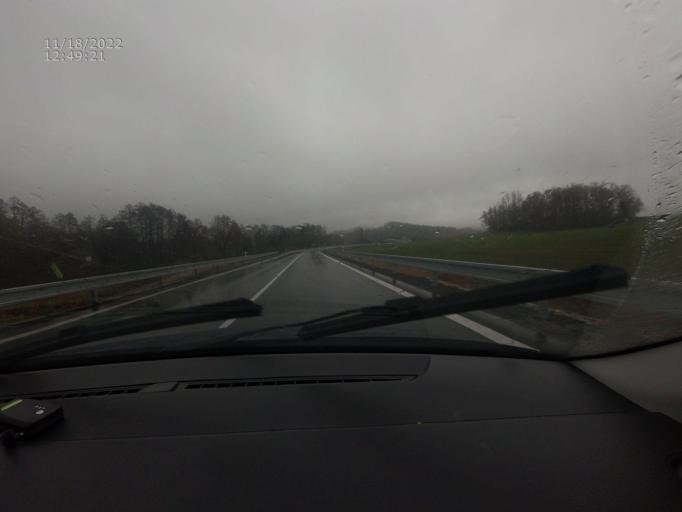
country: CZ
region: Plzensky
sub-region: Okres Klatovy
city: Kolinec
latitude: 49.3263
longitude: 13.4406
